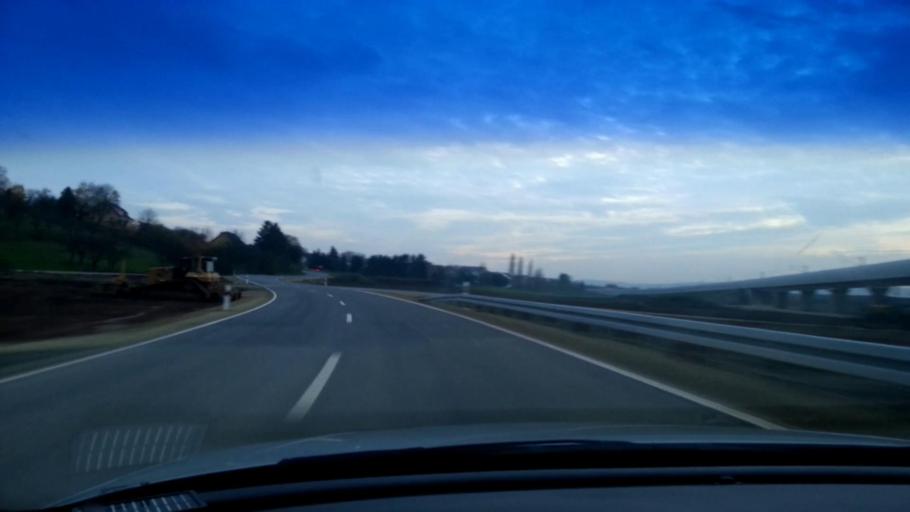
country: DE
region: Bavaria
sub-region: Upper Franconia
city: Breitengussbach
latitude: 49.9818
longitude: 10.8955
